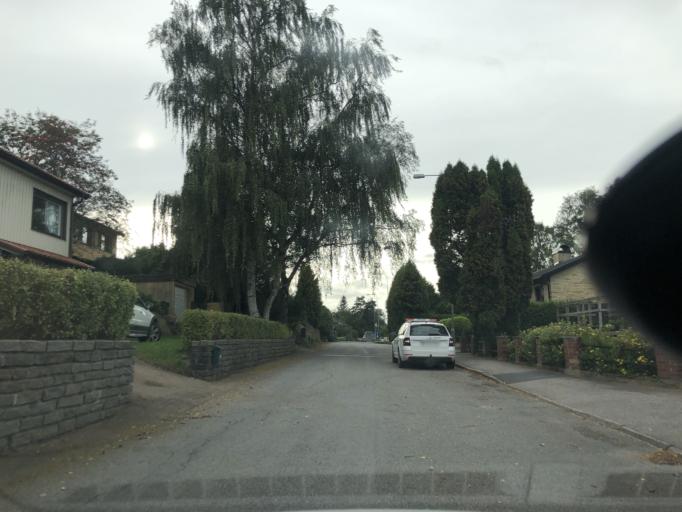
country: SE
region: Vaestra Goetaland
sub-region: Goteborg
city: Goeteborg
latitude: 57.7536
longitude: 11.9646
